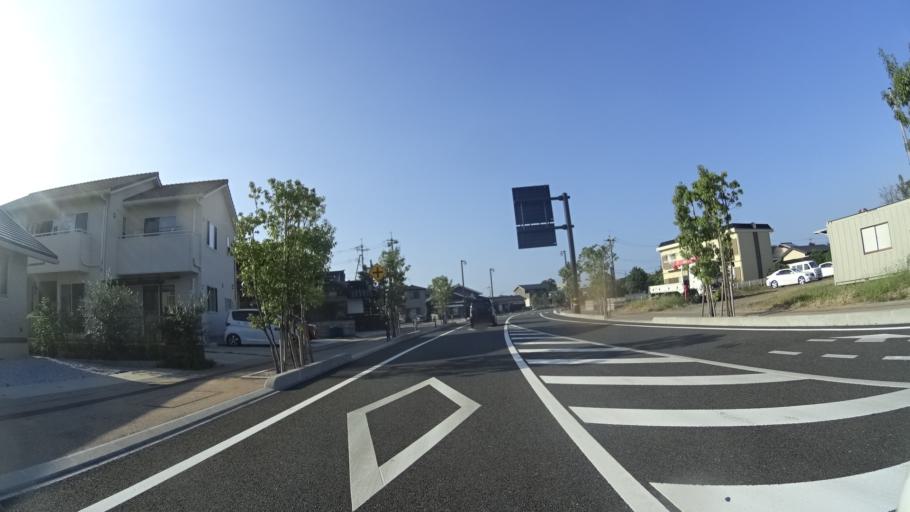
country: JP
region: Yamaguchi
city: Hagi
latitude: 34.4079
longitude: 131.3915
